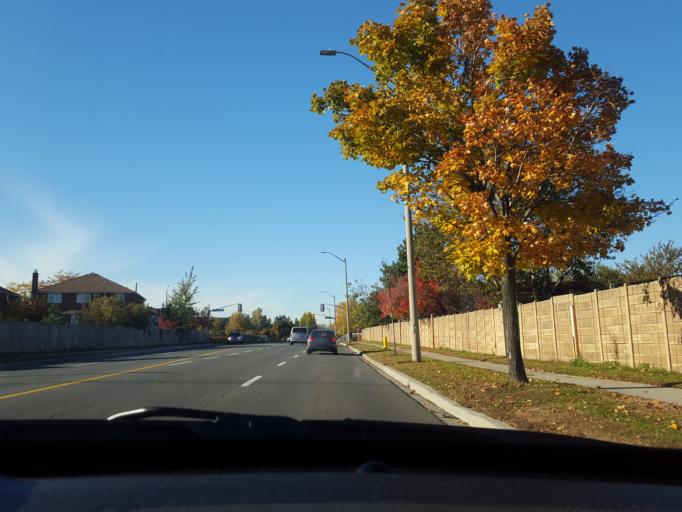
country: CA
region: Ontario
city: Markham
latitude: 43.8409
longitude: -79.2916
